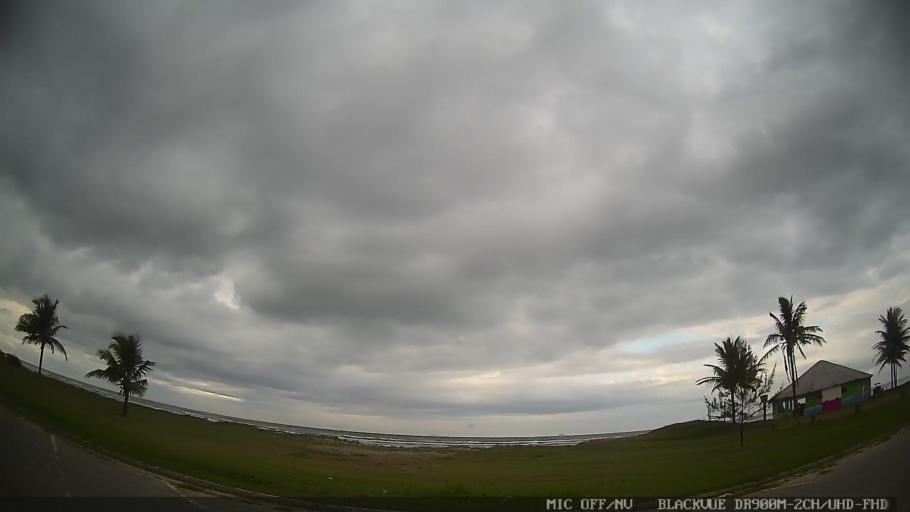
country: BR
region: Sao Paulo
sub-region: Itanhaem
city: Itanhaem
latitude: -24.2271
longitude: -46.8612
